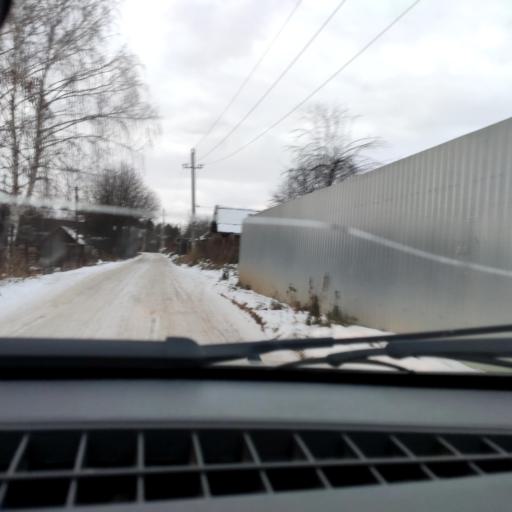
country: RU
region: Bashkortostan
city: Avdon
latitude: 54.6805
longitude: 55.7915
